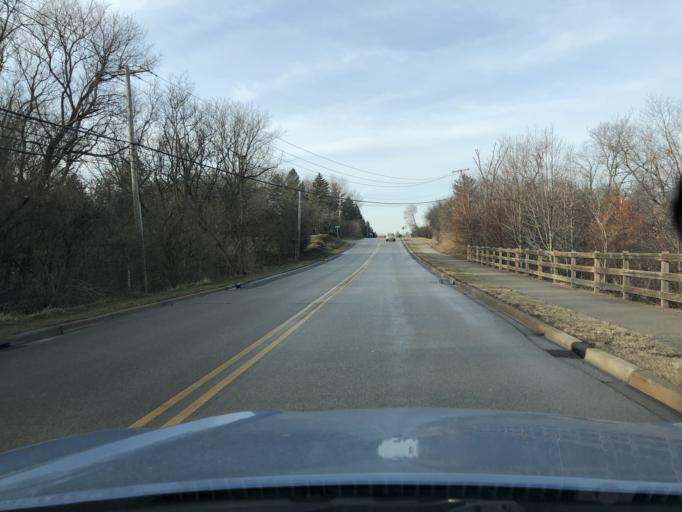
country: US
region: Illinois
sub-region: McHenry County
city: Algonquin
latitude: 42.1574
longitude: -88.3123
